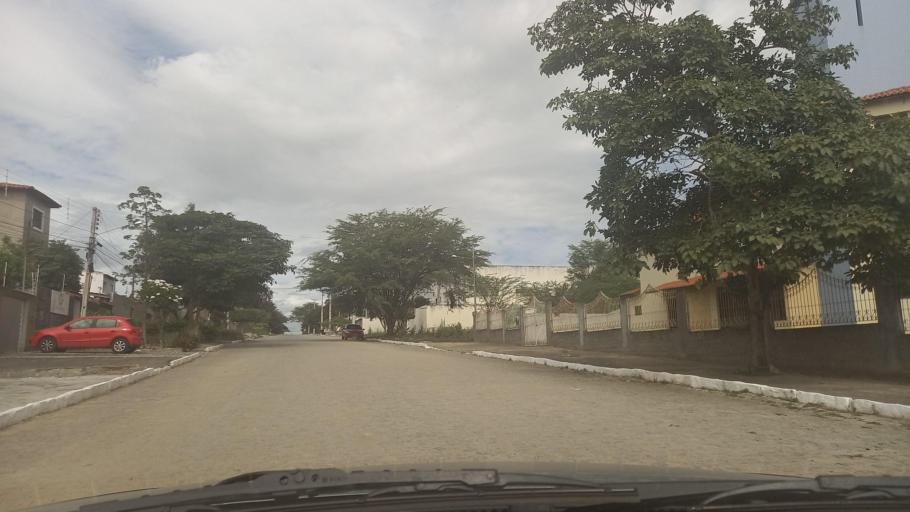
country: BR
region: Pernambuco
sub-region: Caruaru
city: Caruaru
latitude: -8.2944
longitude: -35.9917
